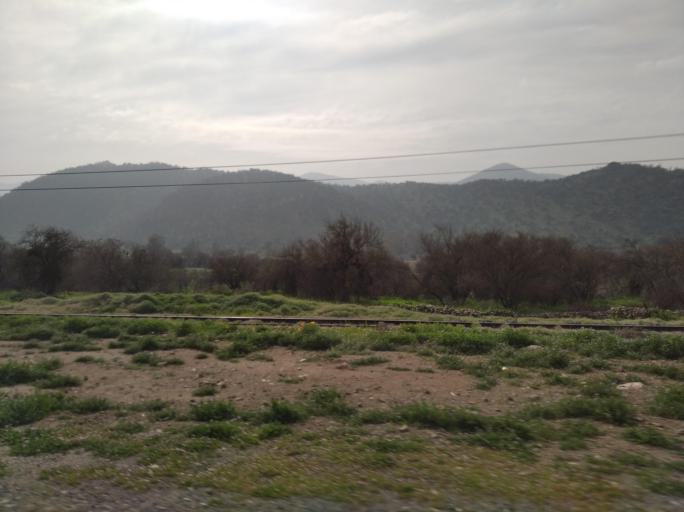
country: CL
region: Santiago Metropolitan
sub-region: Provincia de Chacabuco
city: Lampa
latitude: -33.1426
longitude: -70.9154
